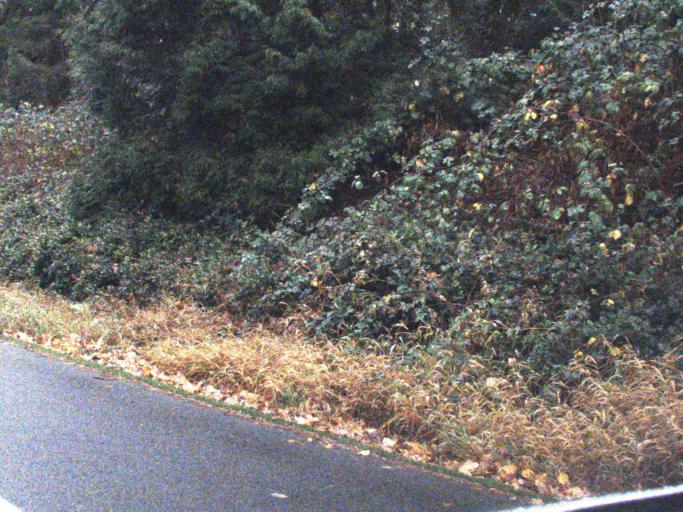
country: US
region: Washington
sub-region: Snohomish County
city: Fobes Hill
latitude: 47.9615
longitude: -122.1019
